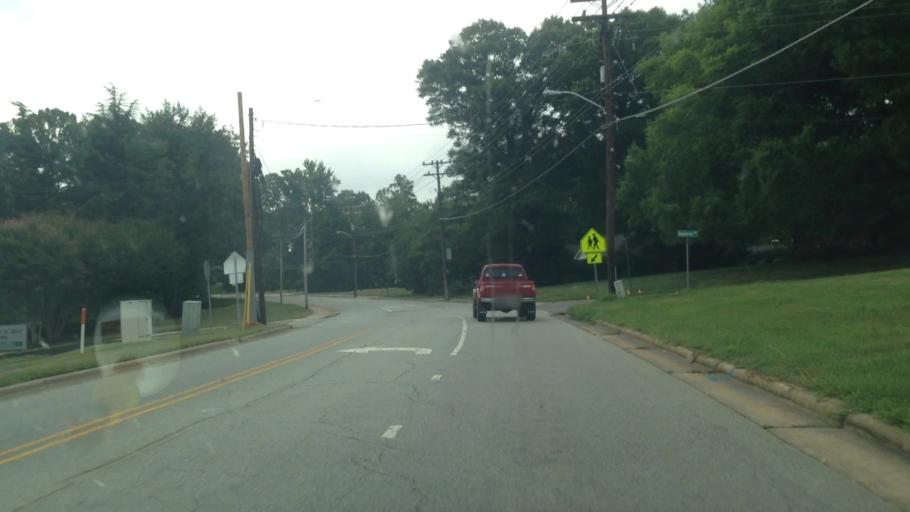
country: US
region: North Carolina
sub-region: Forsyth County
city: Kernersville
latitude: 36.1270
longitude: -80.0838
